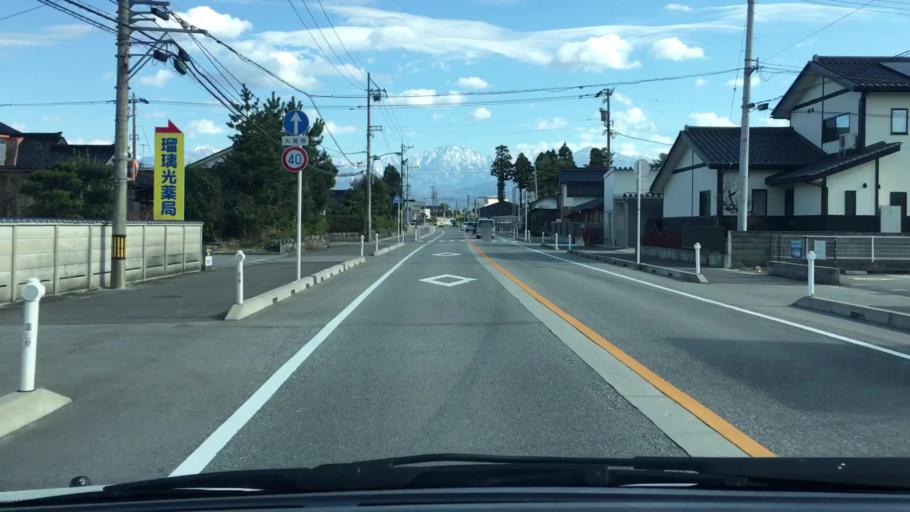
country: JP
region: Toyama
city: Toyama-shi
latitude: 36.7027
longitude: 137.2670
